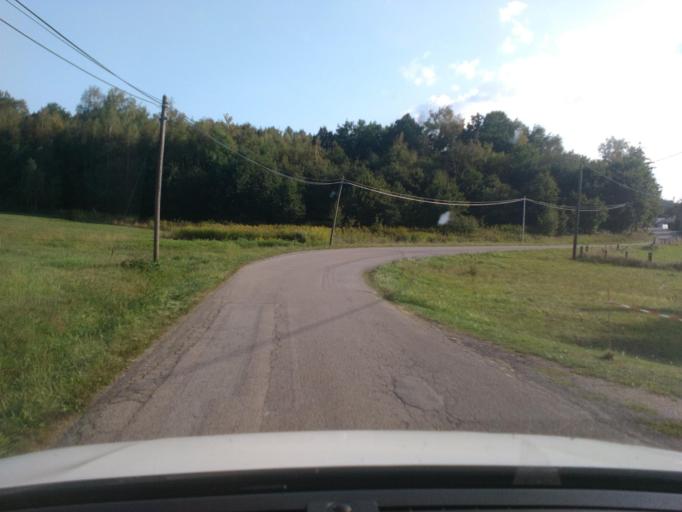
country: FR
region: Lorraine
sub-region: Departement des Vosges
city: Moyenmoutier
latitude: 48.3827
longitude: 6.8946
